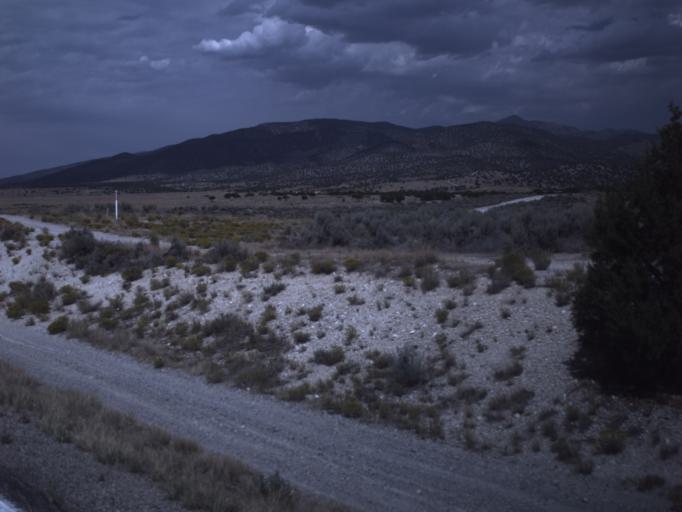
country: US
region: Utah
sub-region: Utah County
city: Eagle Mountain
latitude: 40.2392
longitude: -112.2030
